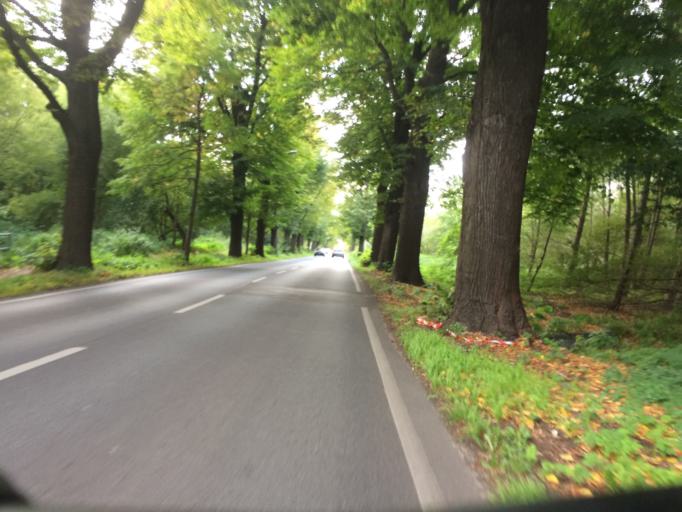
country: DE
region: Berlin
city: Blankenburg
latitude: 52.6168
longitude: 13.4577
